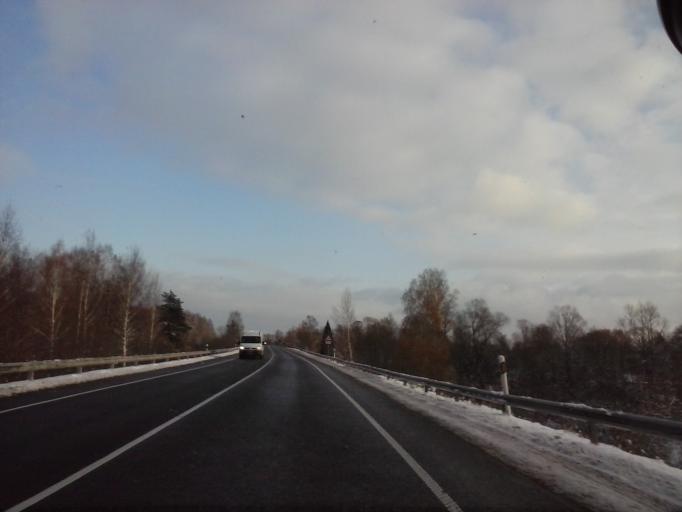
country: EE
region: Tartu
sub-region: Tartu linn
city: Tartu
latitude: 58.3579
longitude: 26.8987
